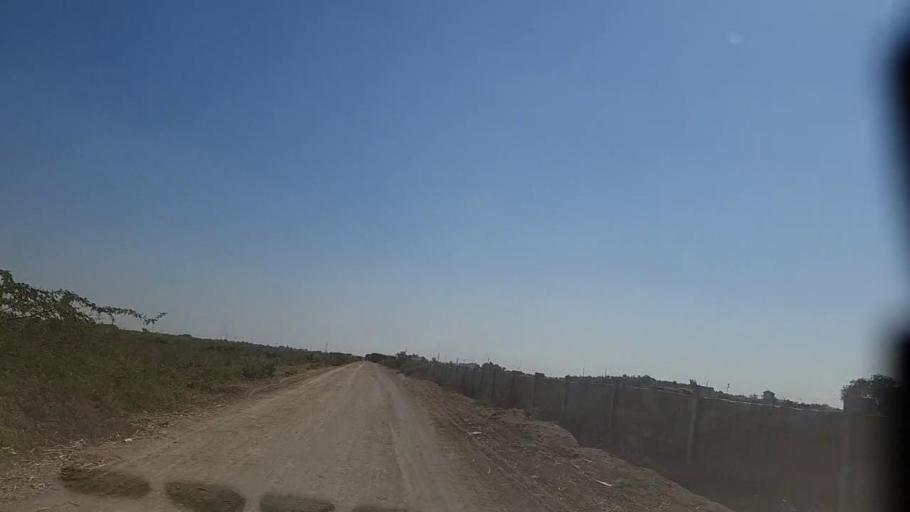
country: PK
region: Sindh
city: Digri
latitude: 25.1648
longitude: 69.0368
